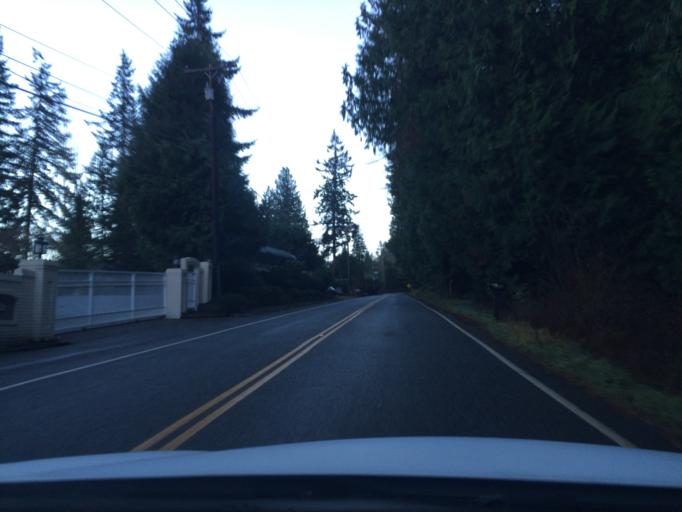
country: US
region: Washington
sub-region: Whatcom County
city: Sudden Valley
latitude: 48.7355
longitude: -122.3564
